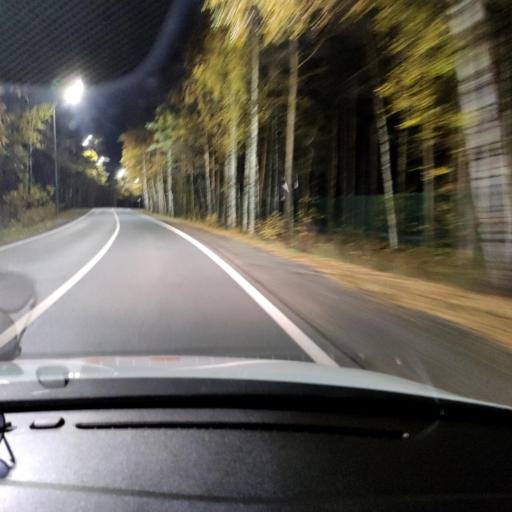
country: RU
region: Tatarstan
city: Verkhniy Uslon
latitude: 55.6343
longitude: 49.0189
